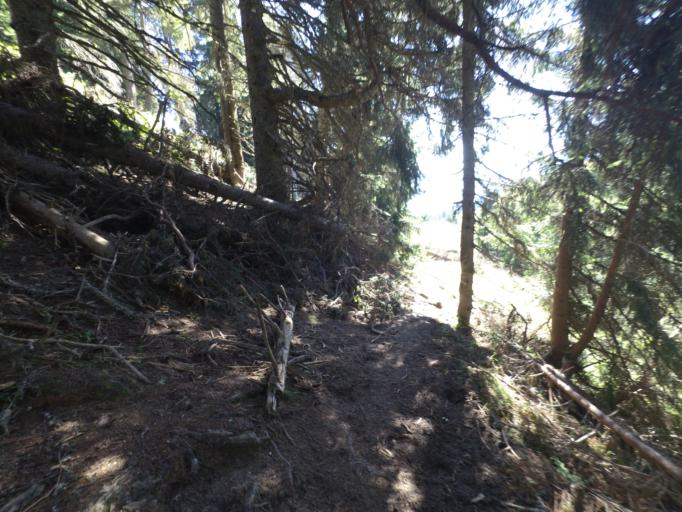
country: AT
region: Salzburg
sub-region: Politischer Bezirk Sankt Johann im Pongau
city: Goldegg
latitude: 47.3597
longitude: 13.0699
